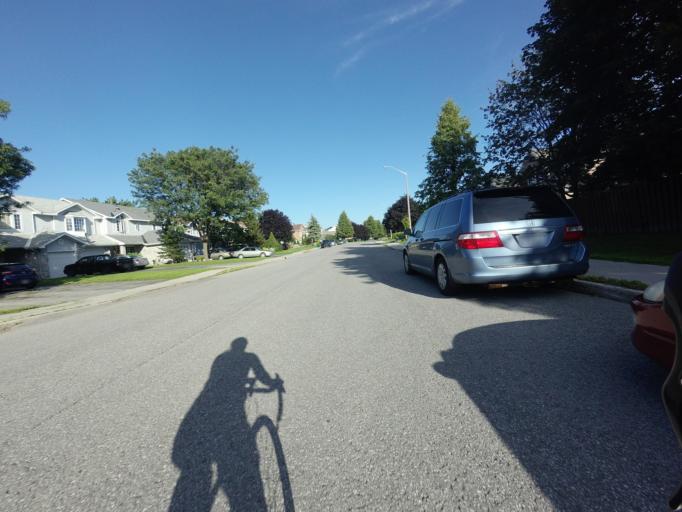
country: CA
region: Ontario
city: Bells Corners
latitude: 45.2932
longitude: -75.7393
